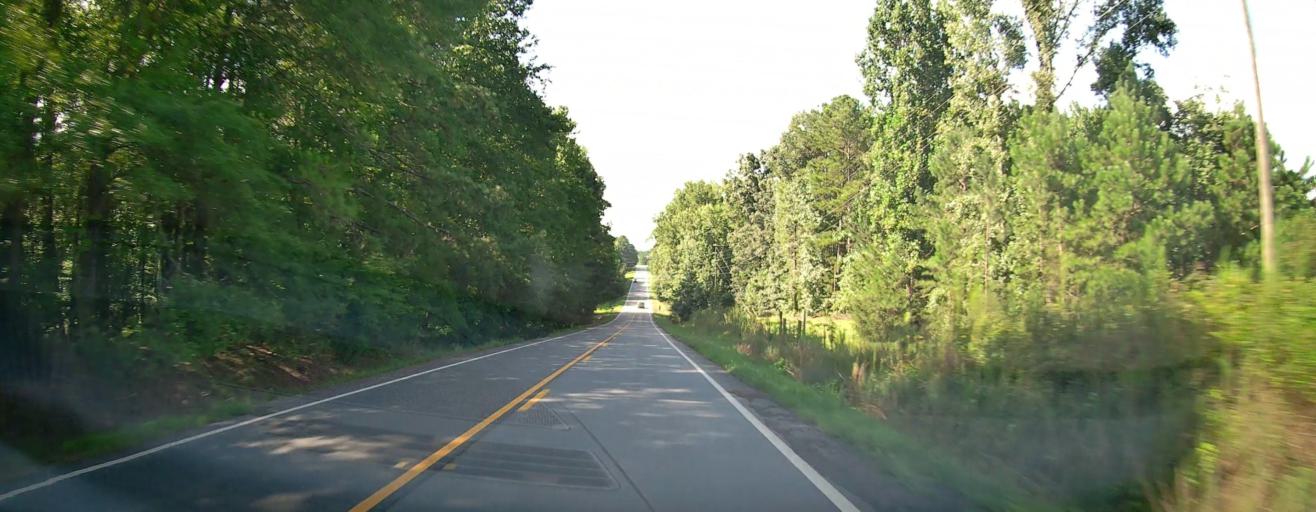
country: US
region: Georgia
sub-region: Upson County
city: Hannahs Mill
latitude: 32.9543
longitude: -84.4605
